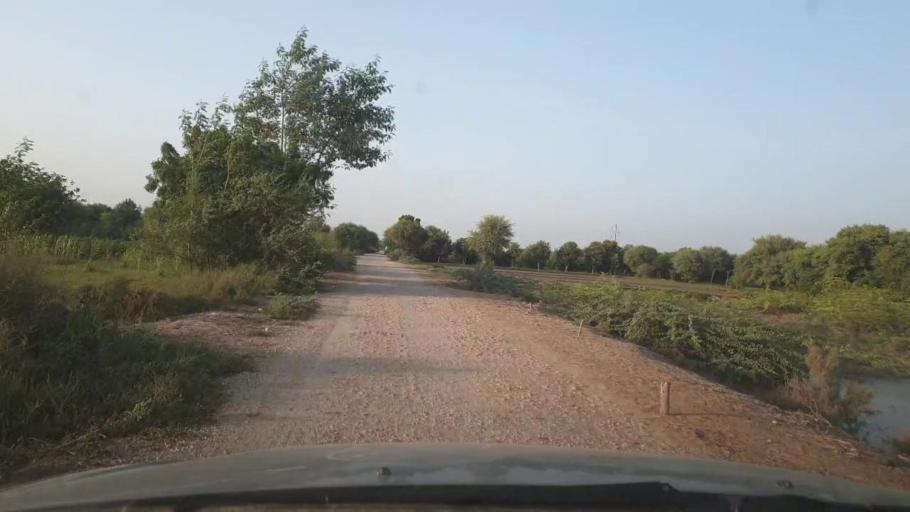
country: PK
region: Sindh
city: Tando Ghulam Ali
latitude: 25.1559
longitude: 68.9747
